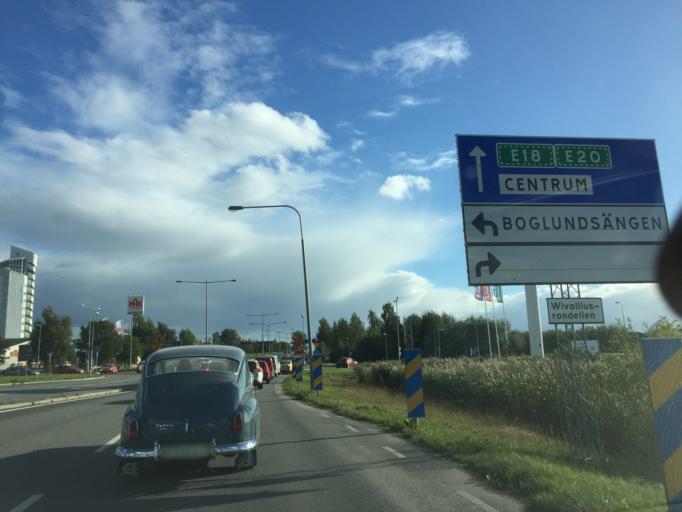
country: SE
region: OErebro
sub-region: Orebro Kommun
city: Orebro
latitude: 59.2983
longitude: 15.2012
